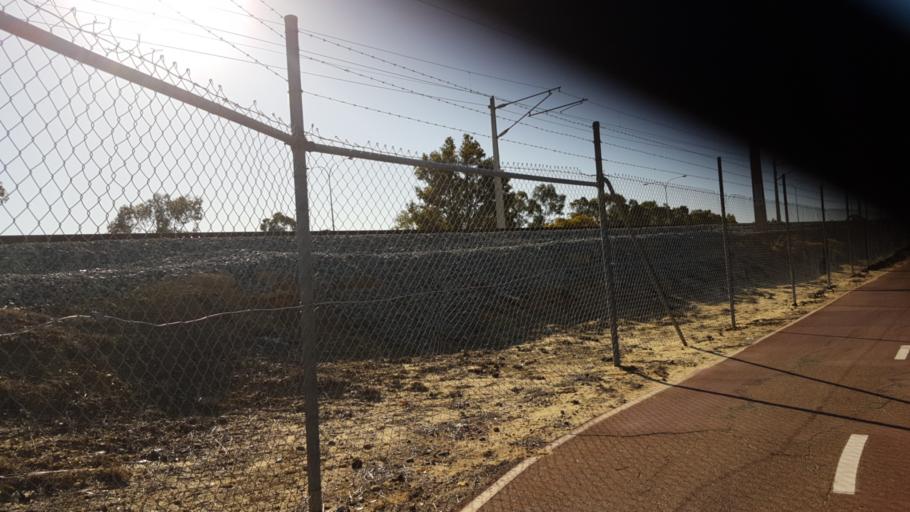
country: AU
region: Western Australia
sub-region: Gosnells
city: Kenwick
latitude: -32.0347
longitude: 115.9680
